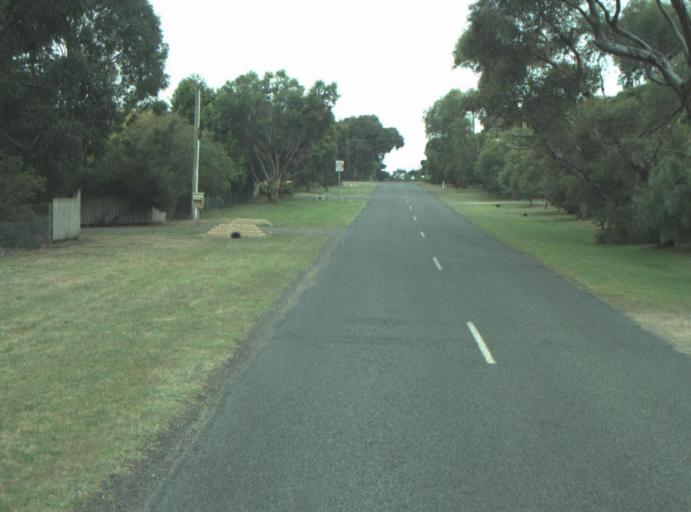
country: AU
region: Victoria
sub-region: Greater Geelong
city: Leopold
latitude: -38.2107
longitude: 144.4341
